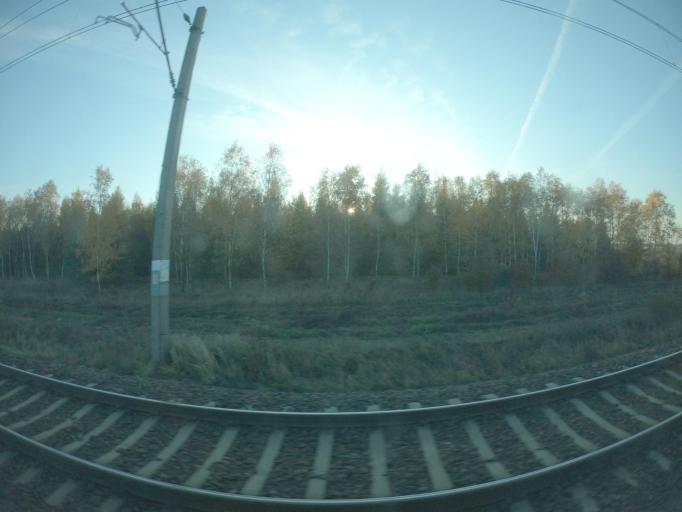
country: PL
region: Lubusz
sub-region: Powiat slubicki
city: Rzepin
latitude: 52.2893
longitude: 14.8907
